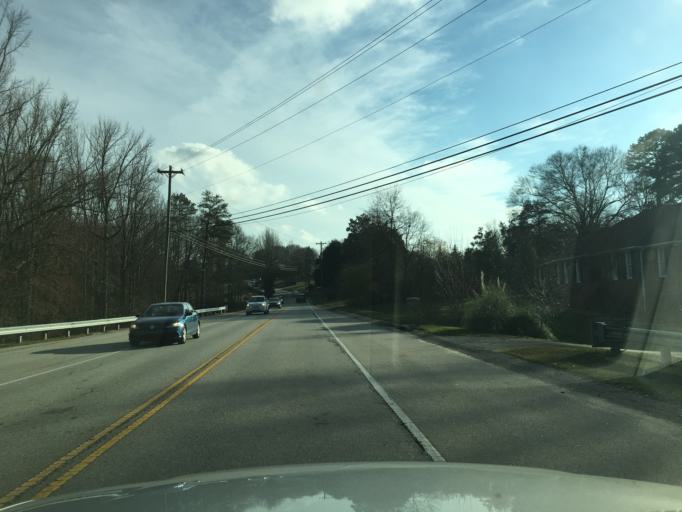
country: US
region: South Carolina
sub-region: Greenville County
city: Taylors
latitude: 34.8833
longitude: -82.2905
